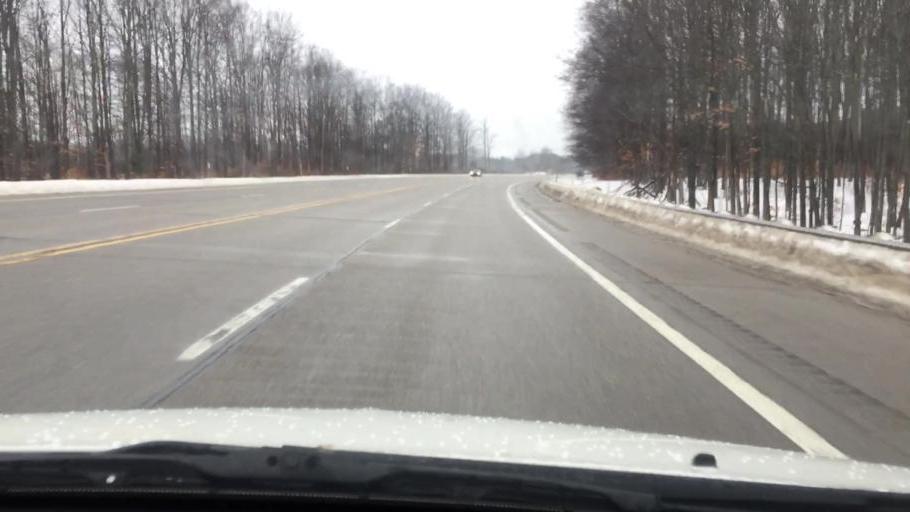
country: US
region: Michigan
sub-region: Kalkaska County
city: Kalkaska
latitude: 44.6152
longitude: -85.3050
